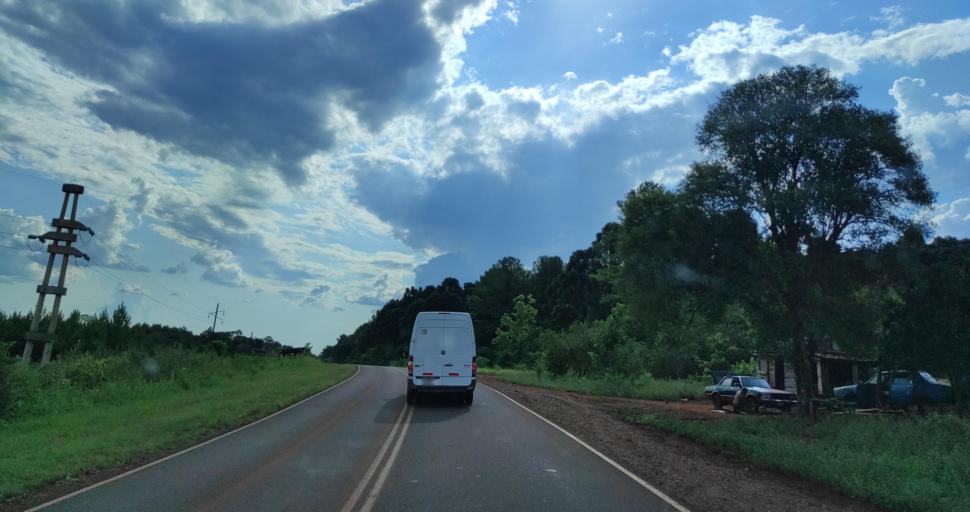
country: AR
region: Misiones
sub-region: Departamento de San Pedro
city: San Pedro
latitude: -26.3468
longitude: -53.9869
